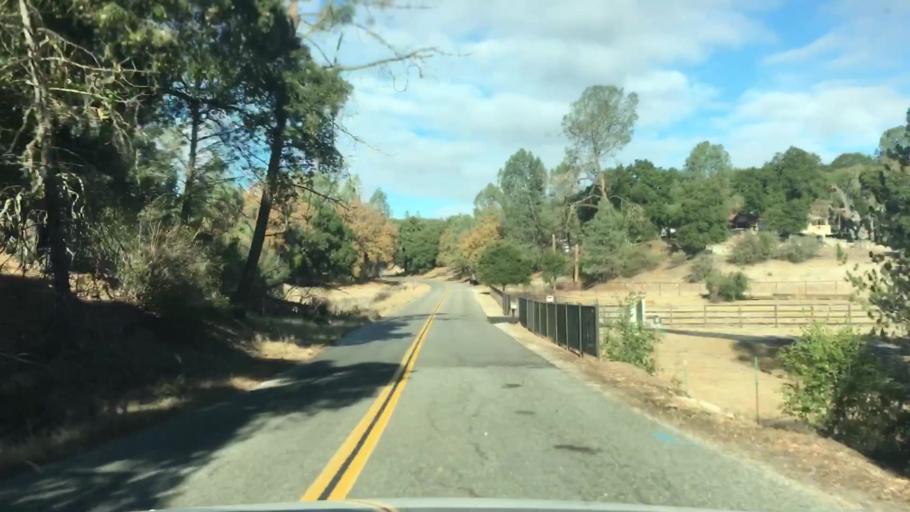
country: US
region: California
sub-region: San Luis Obispo County
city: Atascadero
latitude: 35.4495
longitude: -120.6512
